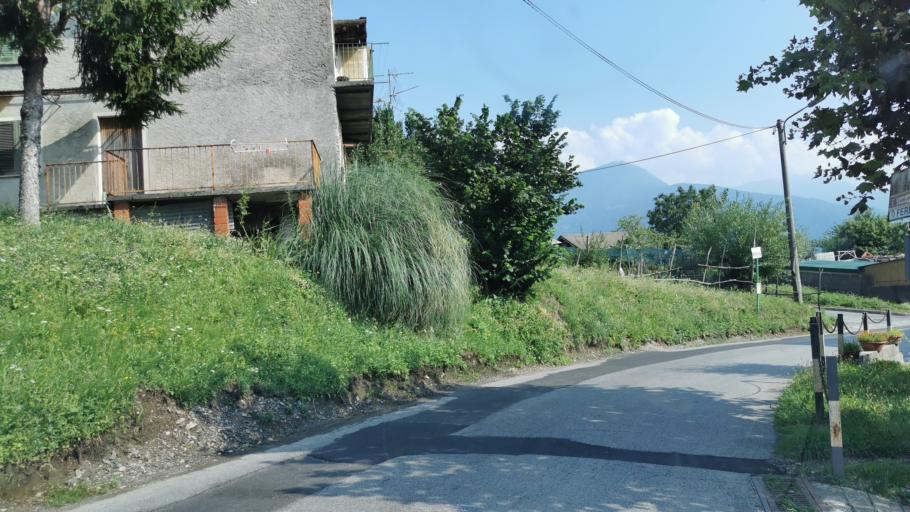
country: IT
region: Lombardy
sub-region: Provincia di Como
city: Peglio
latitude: 46.1539
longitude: 9.2976
